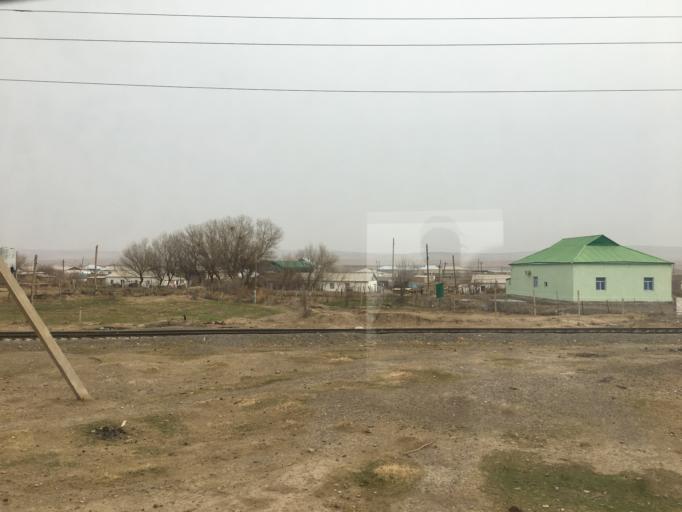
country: TM
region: Mary
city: Serhetabat
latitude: 35.6483
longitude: 62.5547
